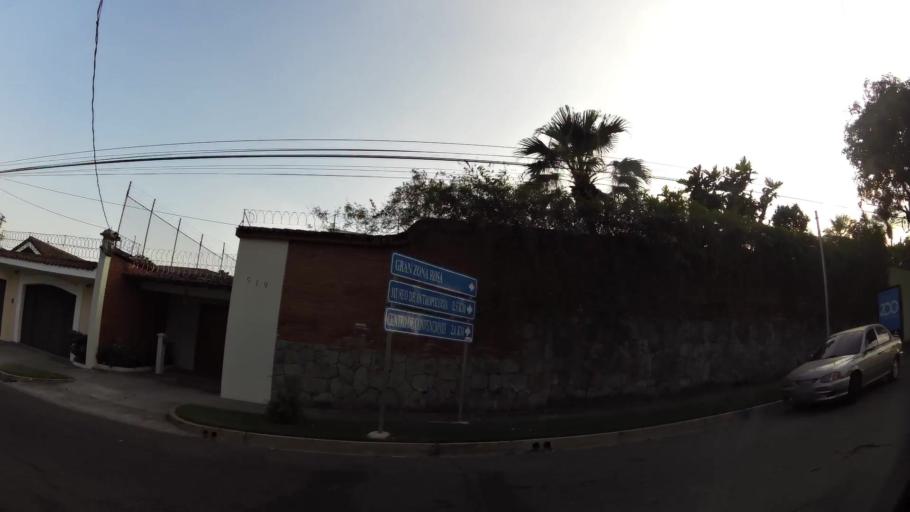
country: SV
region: La Libertad
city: Antiguo Cuscatlan
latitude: 13.6971
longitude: -89.2461
